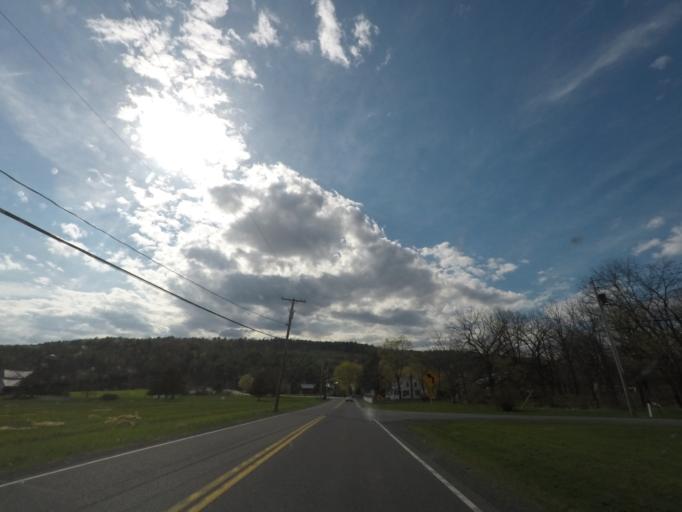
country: US
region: New York
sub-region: Albany County
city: Voorheesville
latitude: 42.5590
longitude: -73.9476
